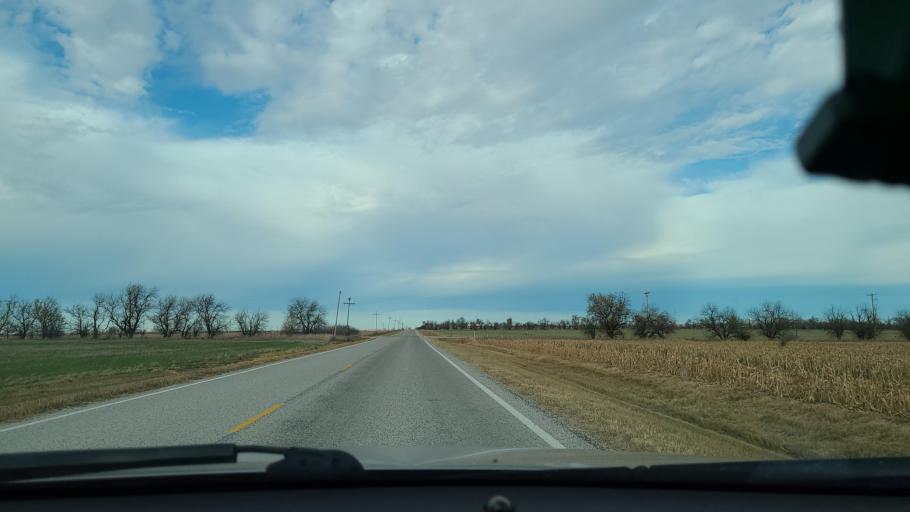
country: US
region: Kansas
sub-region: McPherson County
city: Inman
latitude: 38.3612
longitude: -97.9244
